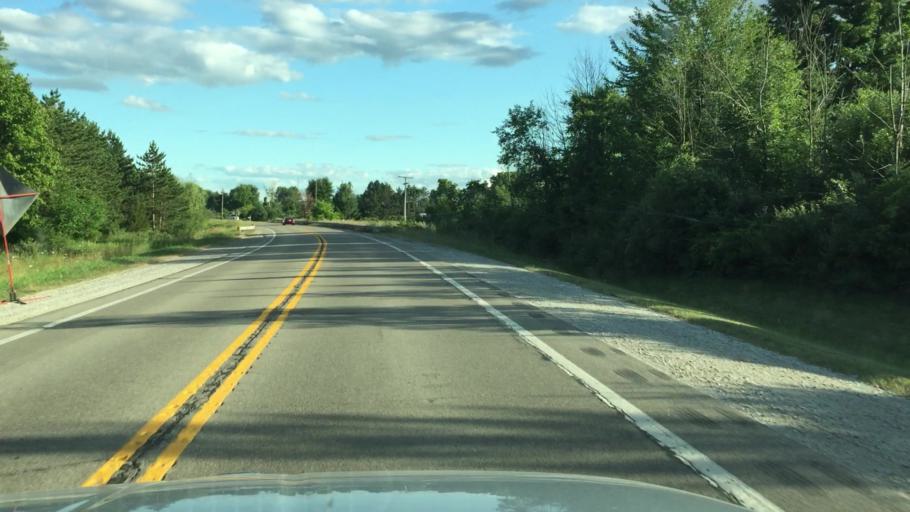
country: US
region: Michigan
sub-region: Saint Clair County
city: Yale
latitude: 43.0667
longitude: -82.7668
